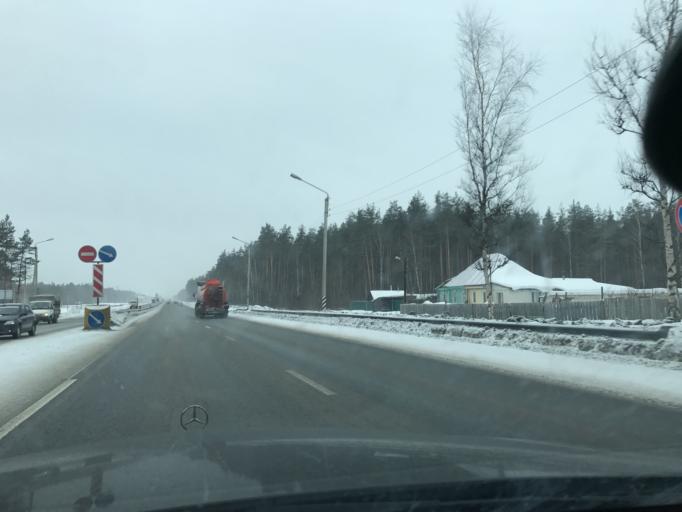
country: RU
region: Nizjnij Novgorod
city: Pyra
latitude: 56.2923
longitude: 43.3320
